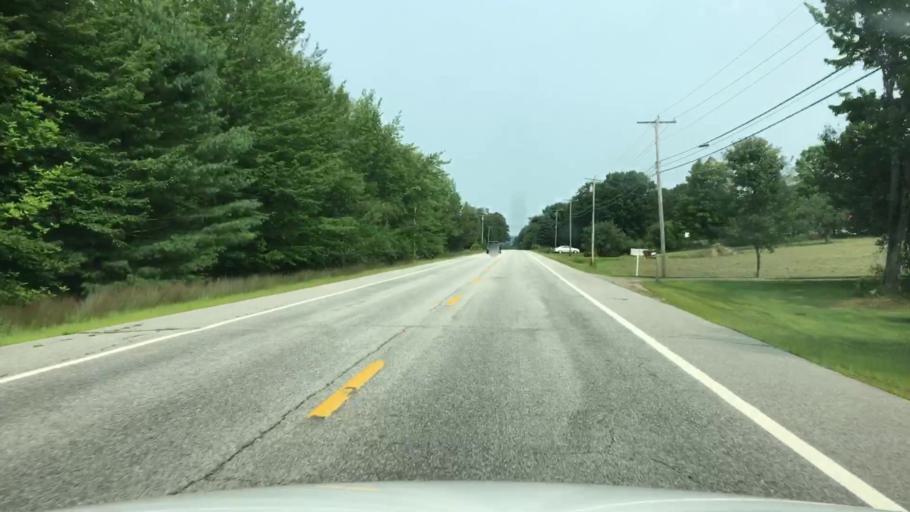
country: US
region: Maine
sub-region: Androscoggin County
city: Livermore Falls
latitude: 44.4348
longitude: -70.1472
